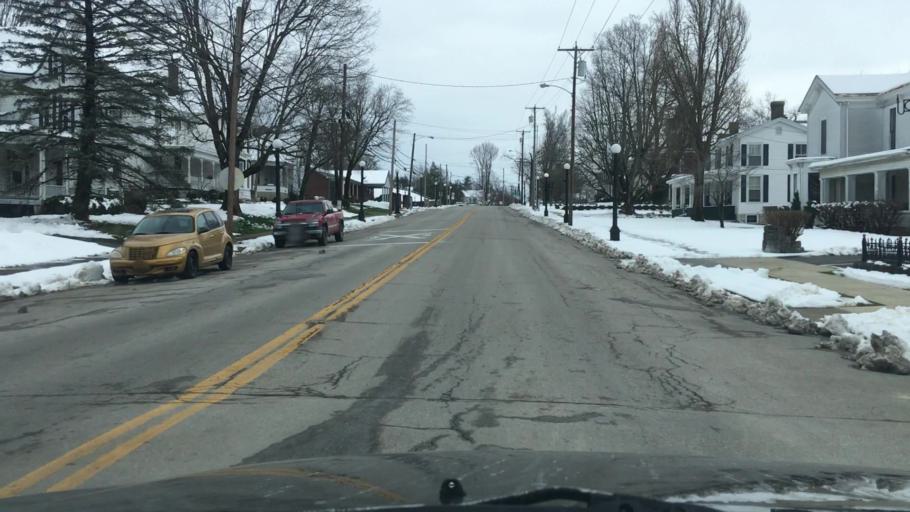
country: US
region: Kentucky
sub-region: Mercer County
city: Harrodsburg
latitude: 37.7622
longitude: -84.8408
